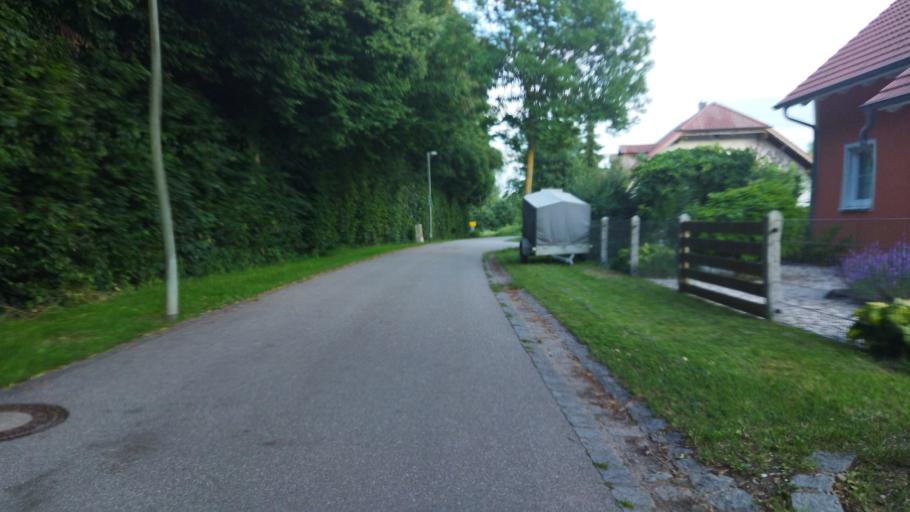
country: DE
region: Bavaria
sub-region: Upper Palatinate
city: Pfatter
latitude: 48.9696
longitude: 12.3384
